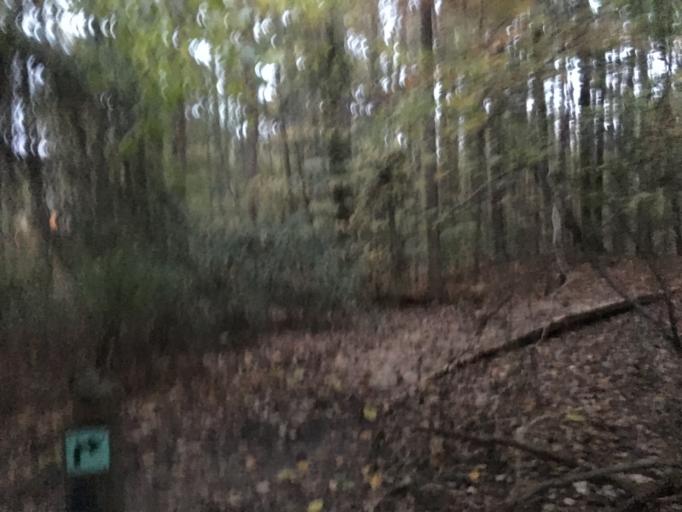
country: US
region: North Carolina
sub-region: Wake County
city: West Raleigh
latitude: 35.8716
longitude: -78.6060
